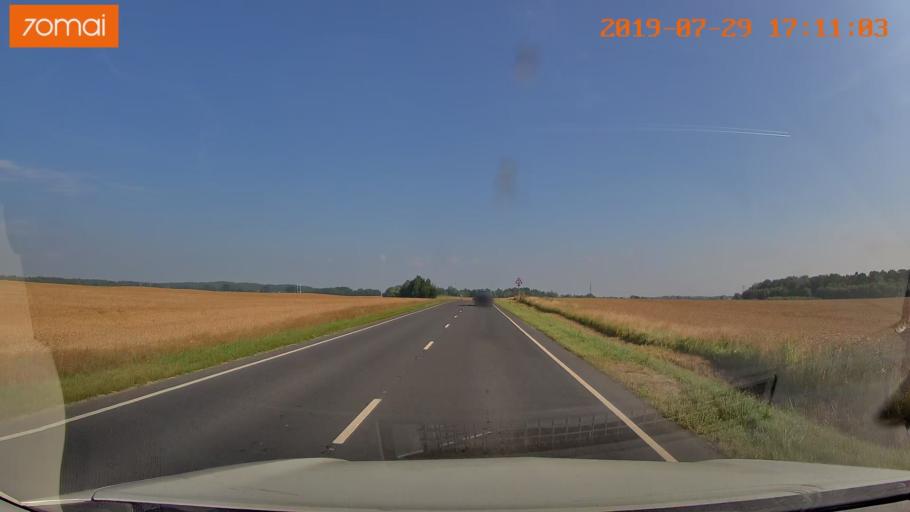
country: RU
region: Kaliningrad
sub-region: Gorod Kaliningrad
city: Kaliningrad
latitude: 54.7978
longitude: 20.3757
